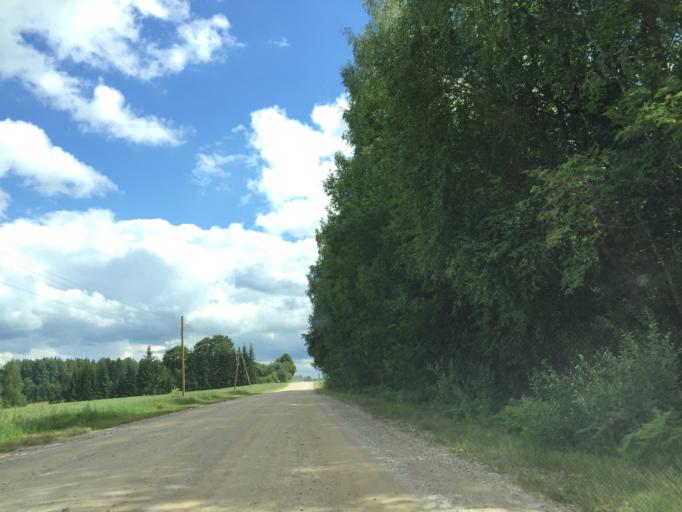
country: LV
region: Malpils
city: Malpils
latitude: 56.8737
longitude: 25.0035
